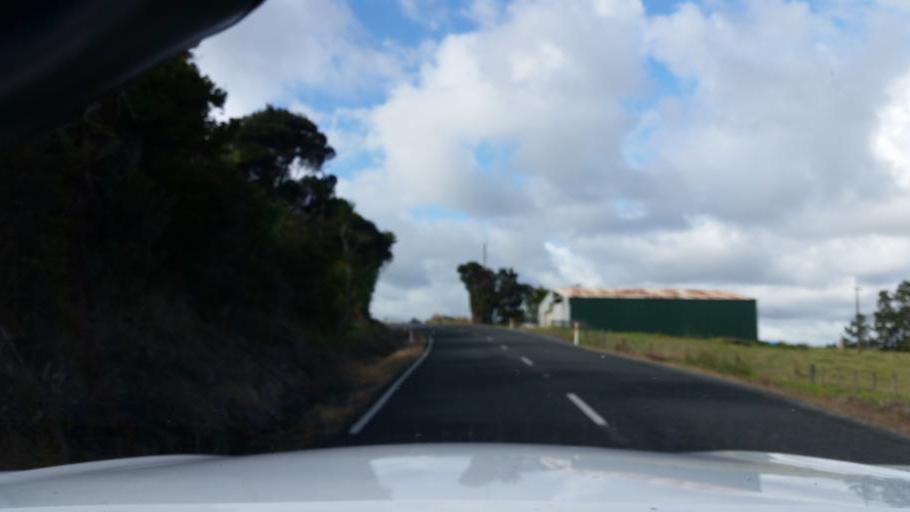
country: NZ
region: Auckland
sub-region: Auckland
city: Wellsford
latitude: -36.0853
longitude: 174.5430
